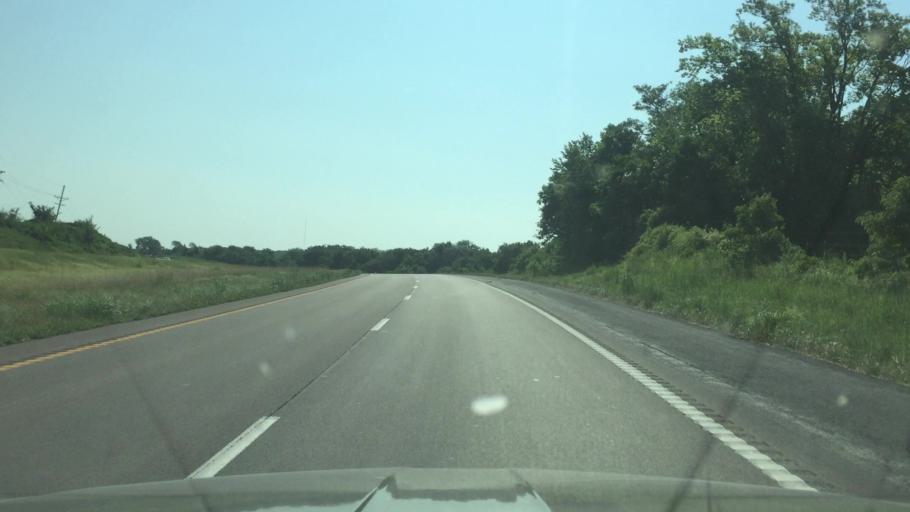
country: US
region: Missouri
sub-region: Johnson County
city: Knob Noster
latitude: 38.7719
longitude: -93.6456
